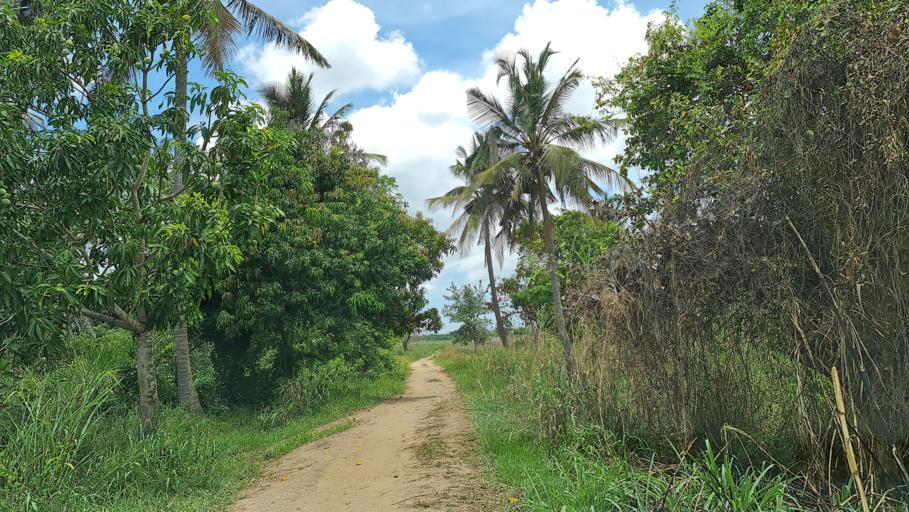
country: MZ
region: Zambezia
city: Quelimane
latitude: -17.5858
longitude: 37.3920
